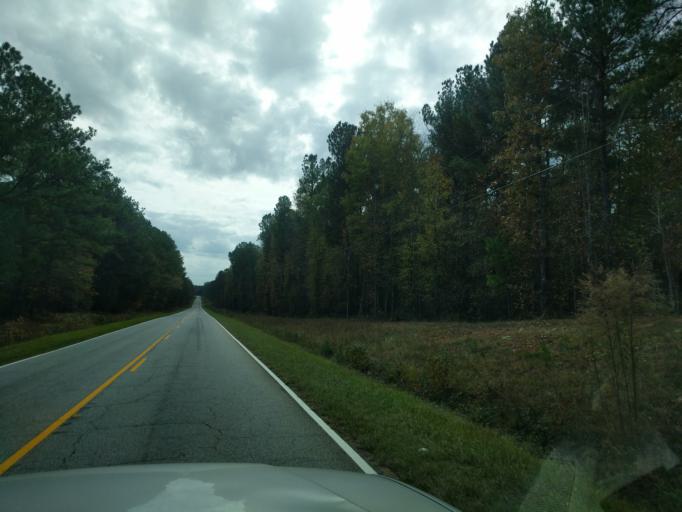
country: US
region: South Carolina
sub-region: Saluda County
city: Saluda
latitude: 34.1374
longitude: -81.8437
